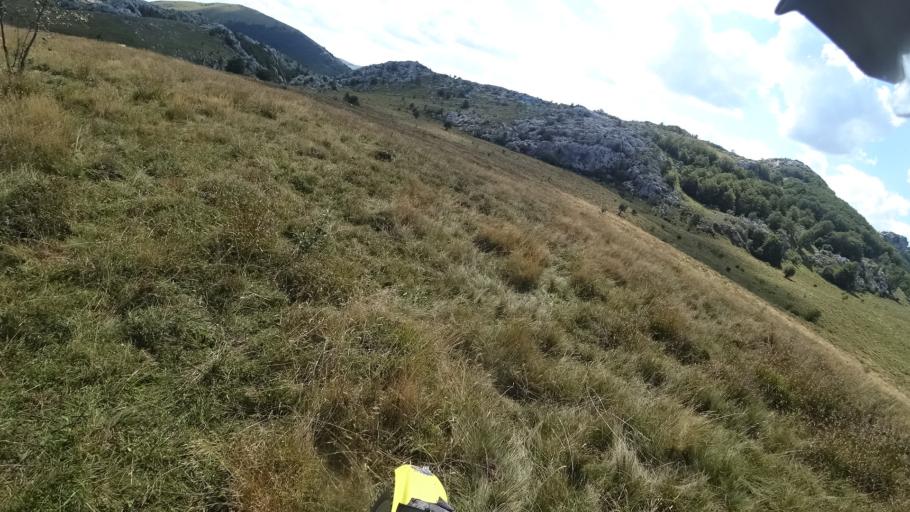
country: HR
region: Zadarska
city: Gracac
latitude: 44.4134
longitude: 15.9998
